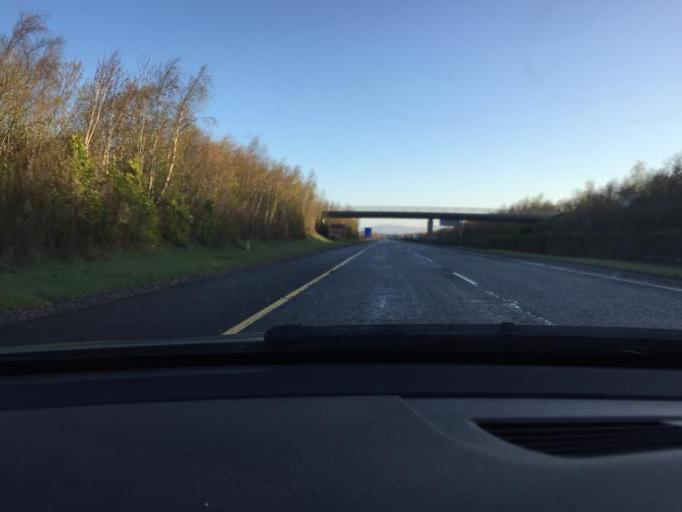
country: IE
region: Leinster
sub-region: Lu
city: Castlebellingham
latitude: 53.8894
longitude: -6.4277
